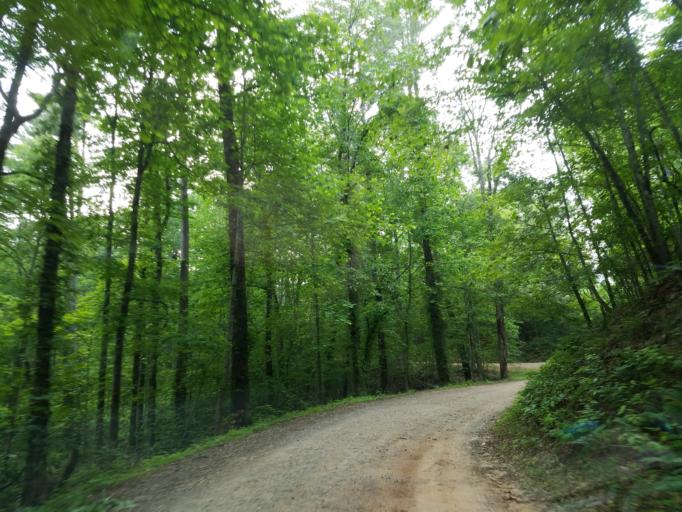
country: US
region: Georgia
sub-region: Lumpkin County
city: Dahlonega
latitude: 34.6040
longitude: -84.1041
